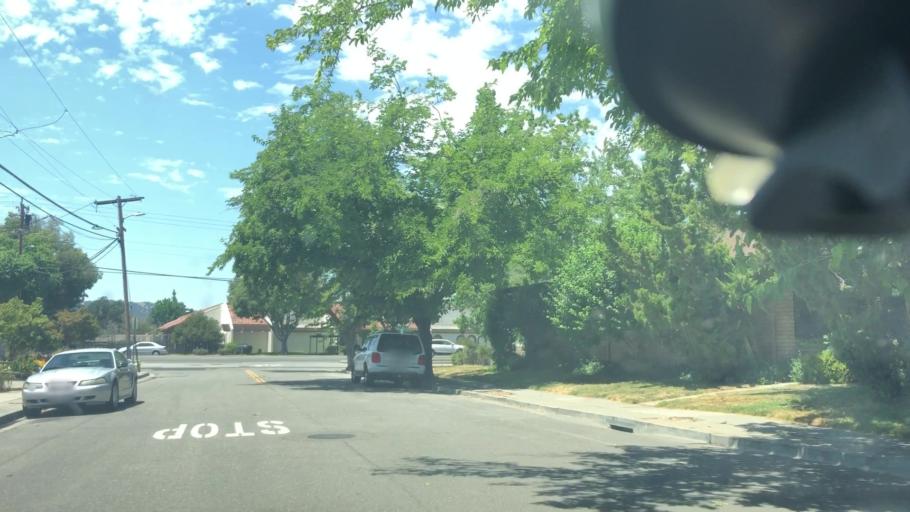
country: US
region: California
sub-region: Alameda County
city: Pleasanton
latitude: 37.6714
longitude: -121.8718
